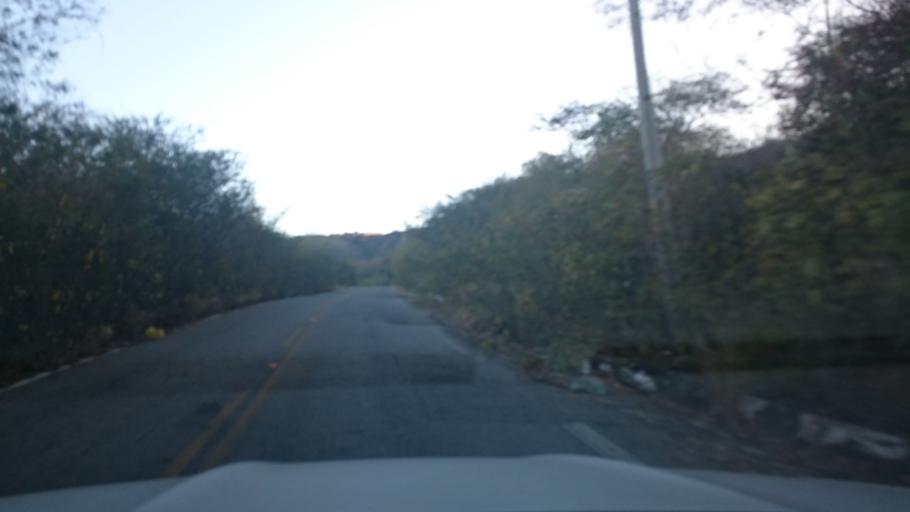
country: BR
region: Rio Grande do Norte
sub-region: Umarizal
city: Umarizal
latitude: -6.0127
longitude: -37.9879
